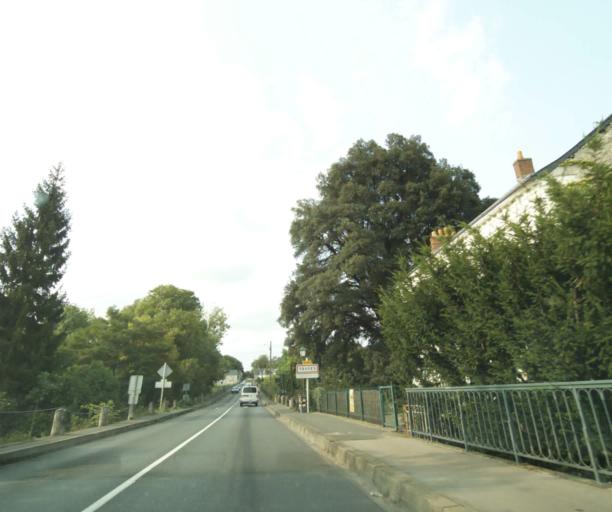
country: FR
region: Centre
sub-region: Departement d'Indre-et-Loire
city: Cormery
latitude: 47.2700
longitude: 0.8347
